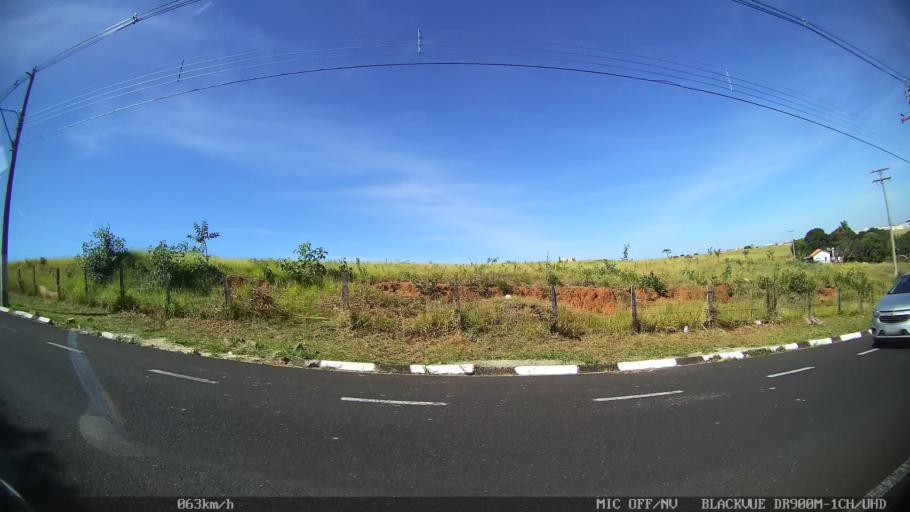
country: BR
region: Sao Paulo
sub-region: Franca
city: Franca
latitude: -20.5287
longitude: -47.3717
